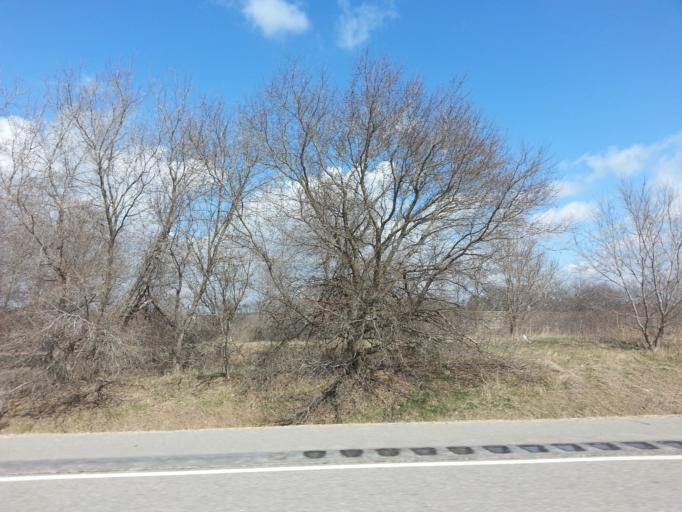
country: US
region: Minnesota
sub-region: Goodhue County
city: Kenyon
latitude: 44.2661
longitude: -92.9791
